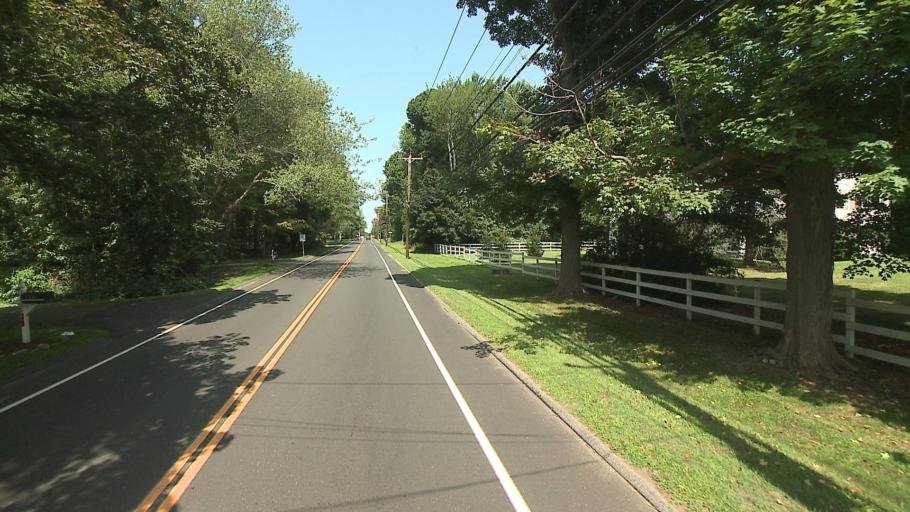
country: US
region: Connecticut
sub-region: Fairfield County
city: Trumbull
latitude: 41.2353
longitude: -73.2666
